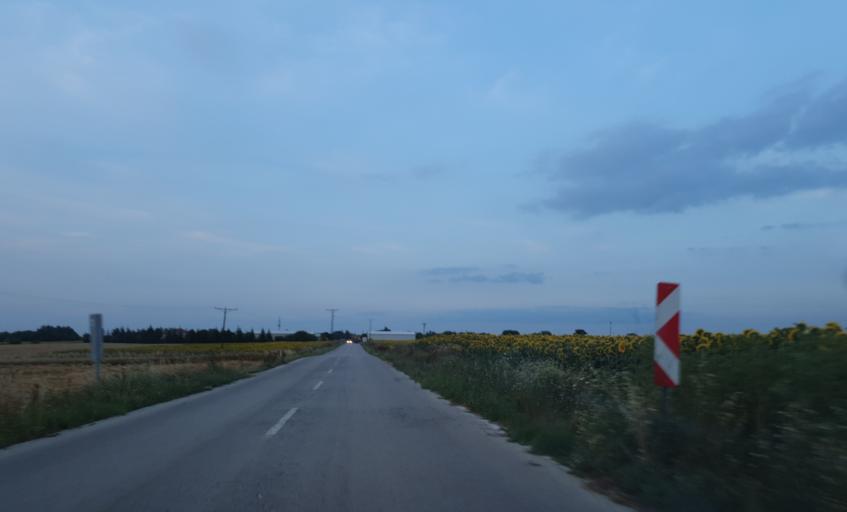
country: TR
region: Tekirdag
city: Beyazkoy
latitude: 41.4069
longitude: 27.6475
